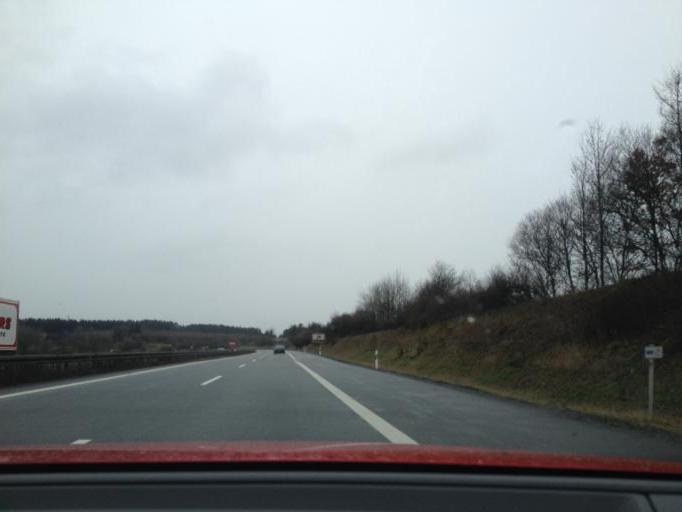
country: DE
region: Bavaria
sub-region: Upper Franconia
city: Schonwald
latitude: 50.2015
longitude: 12.1055
